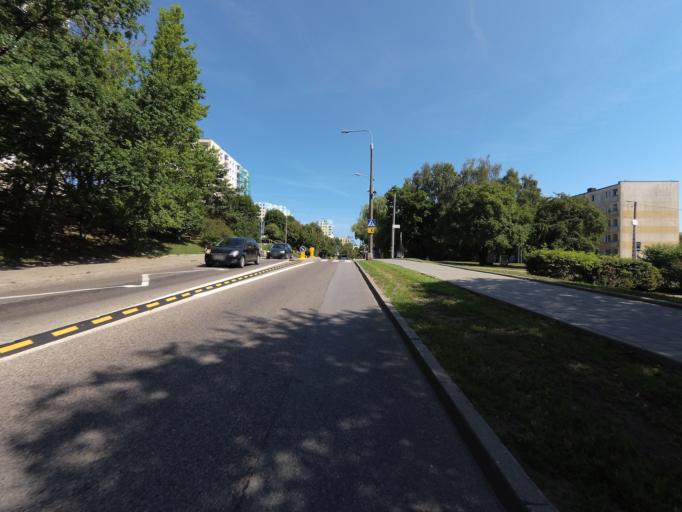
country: PL
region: Pomeranian Voivodeship
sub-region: Gdynia
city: Wielki Kack
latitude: 54.4947
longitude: 18.5080
